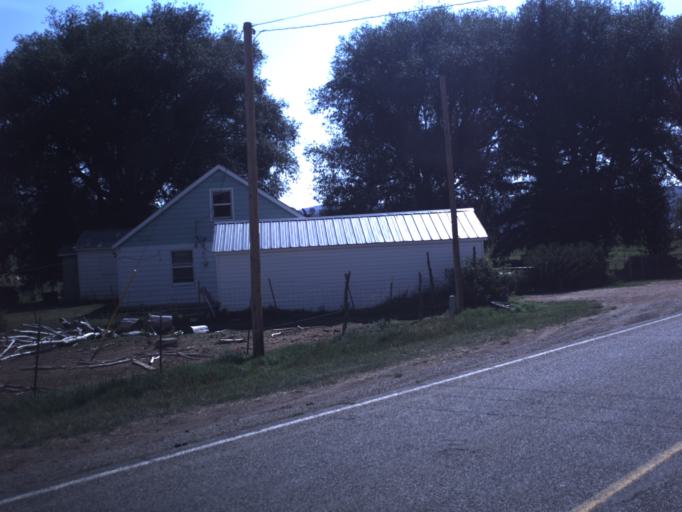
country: US
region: Utah
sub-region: Duchesne County
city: Duchesne
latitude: 40.3490
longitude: -110.7045
